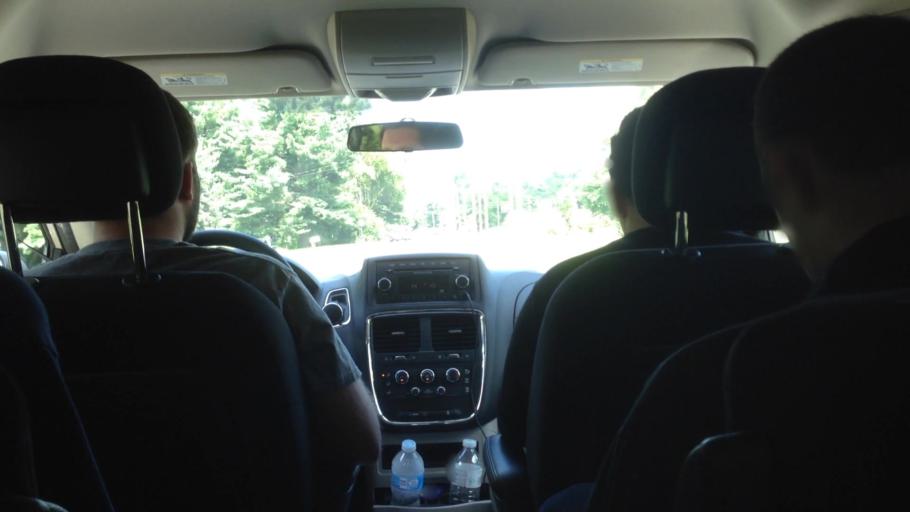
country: US
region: New York
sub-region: Dutchess County
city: Red Hook
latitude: 42.0274
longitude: -73.8475
